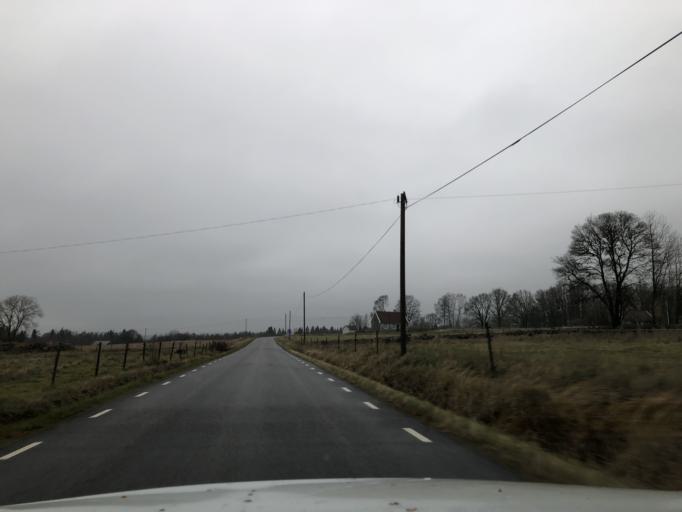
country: SE
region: Vaestra Goetaland
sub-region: Ulricehamns Kommun
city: Ulricehamn
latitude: 57.8395
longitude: 13.3788
